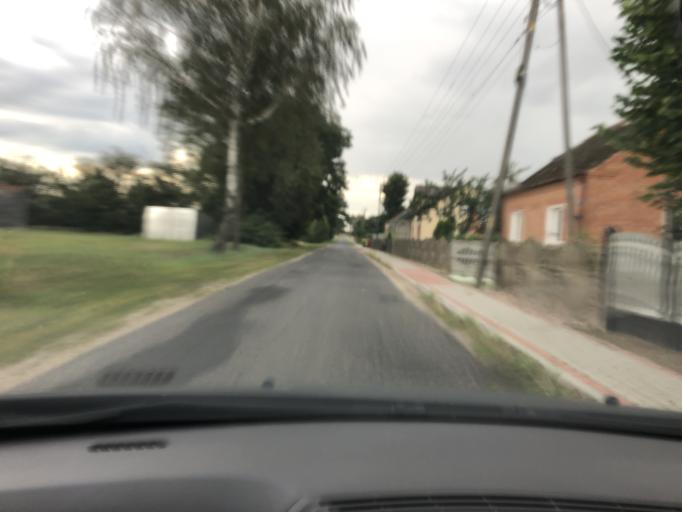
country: PL
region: Lodz Voivodeship
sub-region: Powiat wieruszowski
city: Czastary
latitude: 51.2403
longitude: 18.2926
